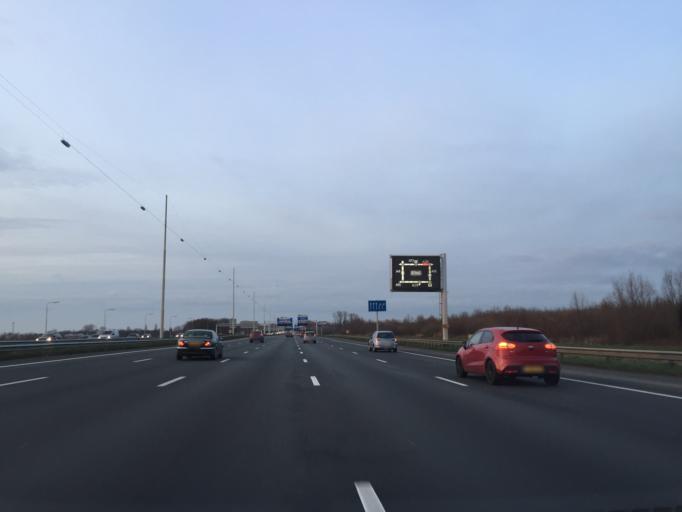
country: NL
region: South Holland
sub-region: Gemeente Hendrik-Ido-Ambacht
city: Hendrik-Ido-Ambacht
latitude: 51.8397
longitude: 4.6144
